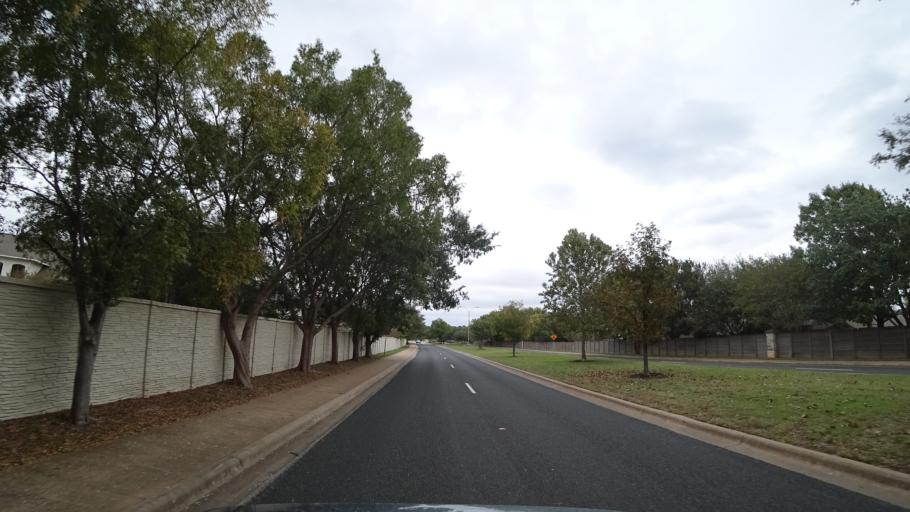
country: US
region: Texas
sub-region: Williamson County
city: Brushy Creek
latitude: 30.5044
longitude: -97.7391
